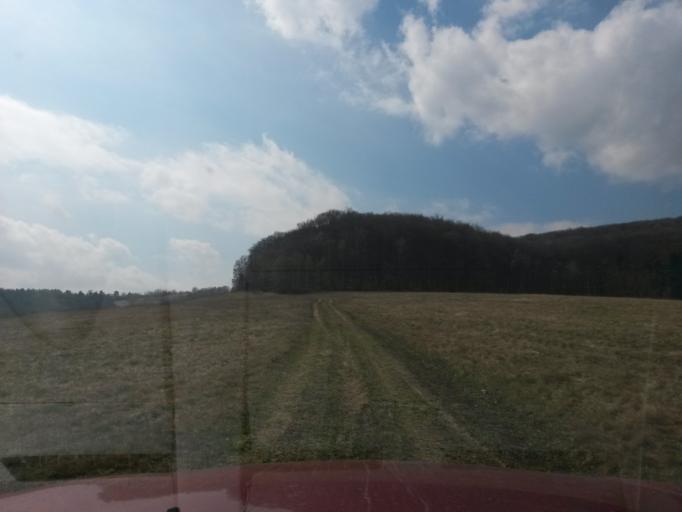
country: SK
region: Presovsky
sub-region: Okres Presov
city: Presov
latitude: 48.9336
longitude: 21.1448
